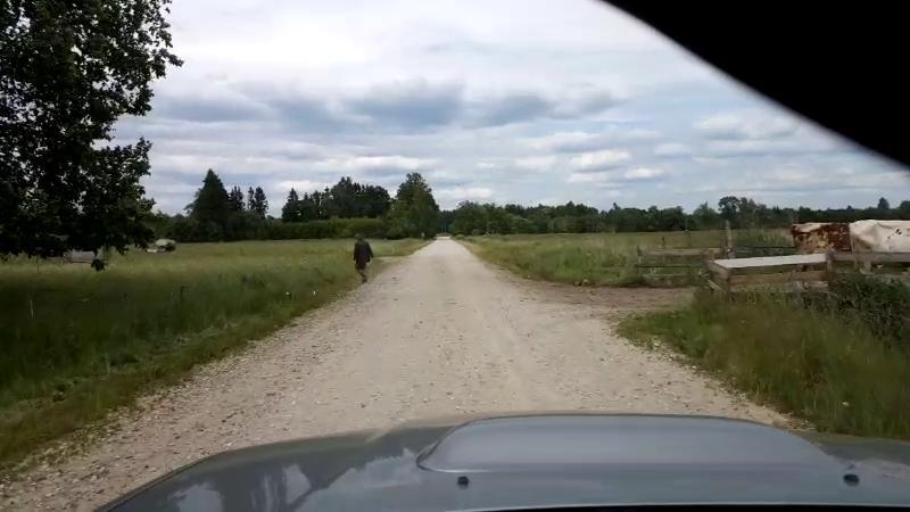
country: EE
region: Paernumaa
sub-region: Sauga vald
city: Sauga
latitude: 58.5113
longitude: 24.5807
